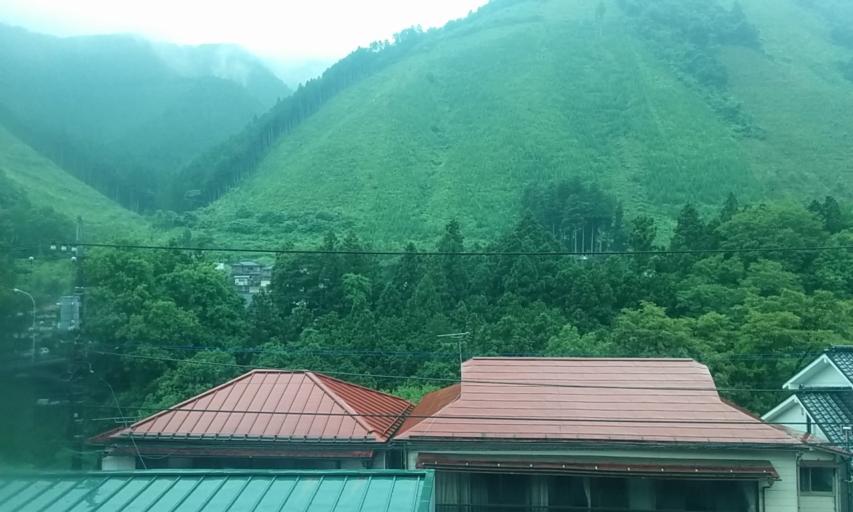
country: JP
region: Tokyo
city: Ome
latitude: 35.8013
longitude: 139.1822
